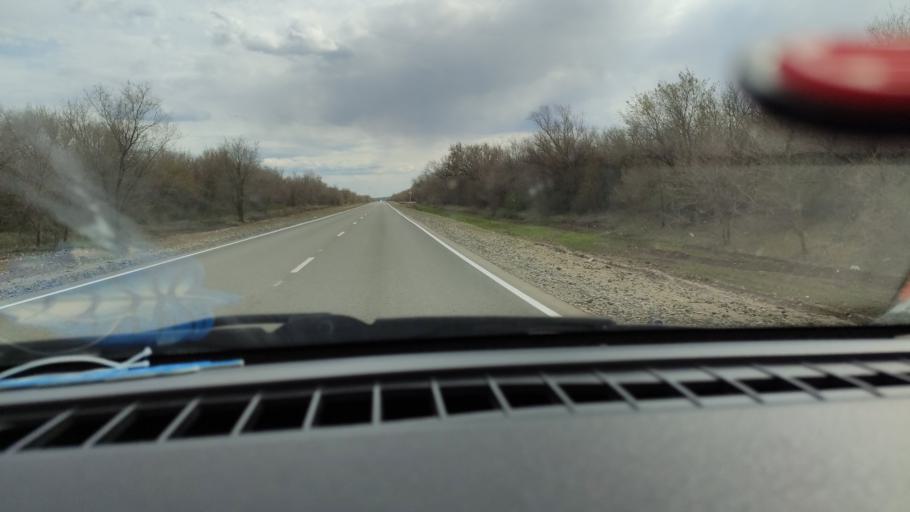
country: RU
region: Saratov
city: Privolzhskiy
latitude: 51.1418
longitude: 45.9602
